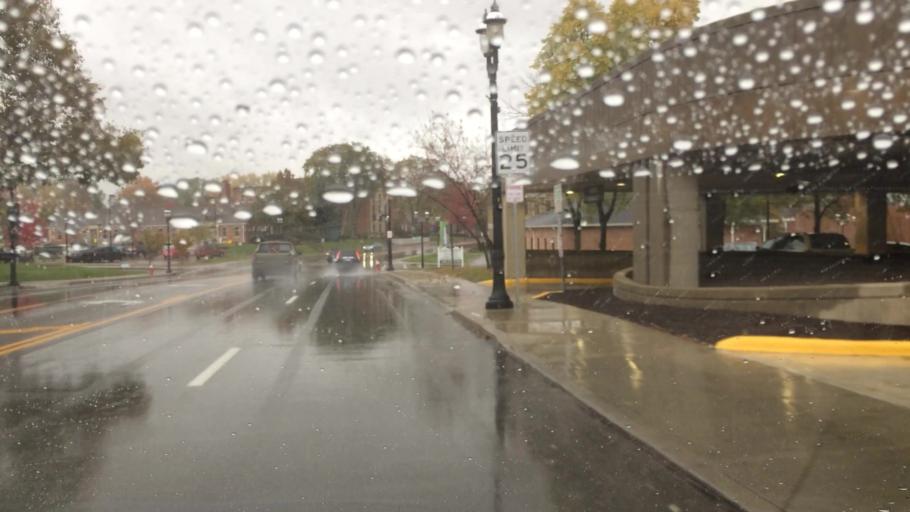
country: US
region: Ohio
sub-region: Summit County
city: Cuyahoga Falls
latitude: 41.1371
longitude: -81.4841
